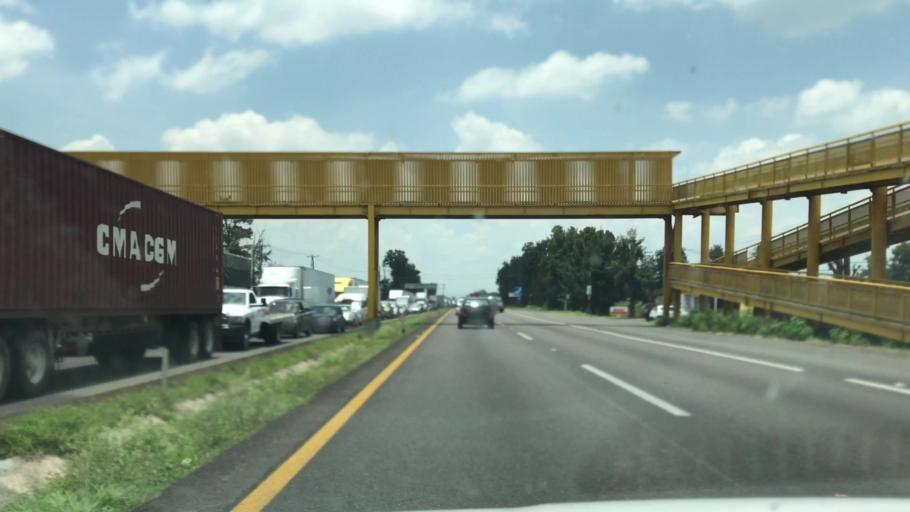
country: MX
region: Guanajuato
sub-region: Irapuato
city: Colonia Morelos de Guadalupe de Rivera
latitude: 20.5973
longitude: -101.4198
